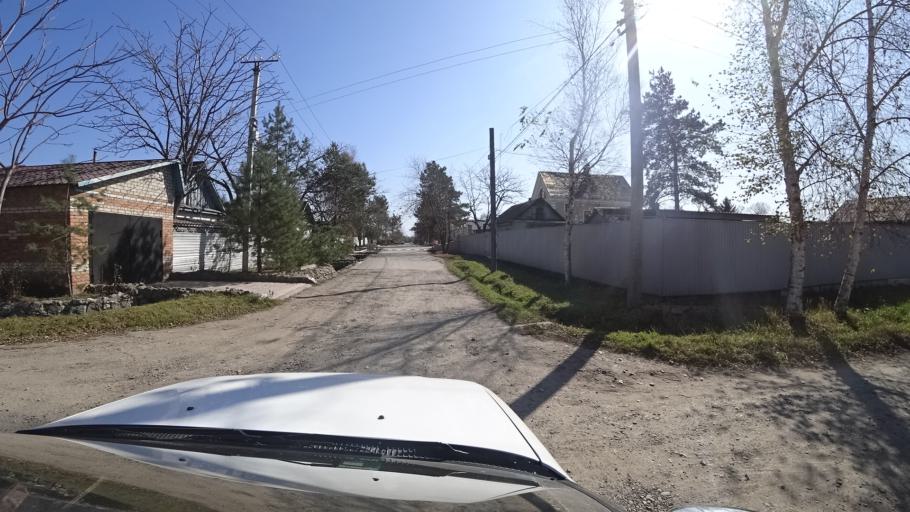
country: RU
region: Primorskiy
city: Dal'nerechensk
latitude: 45.9298
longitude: 133.7480
